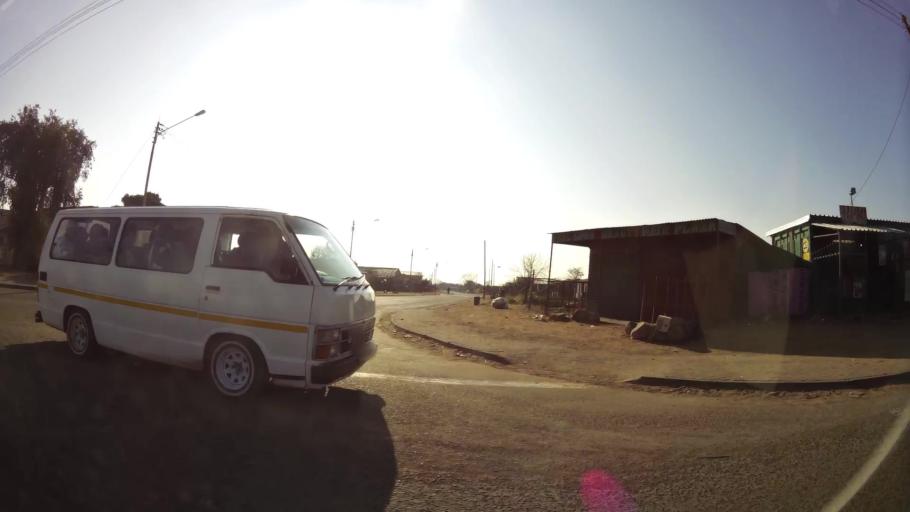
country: ZA
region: Orange Free State
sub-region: Mangaung Metropolitan Municipality
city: Bloemfontein
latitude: -29.1493
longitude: 26.2510
